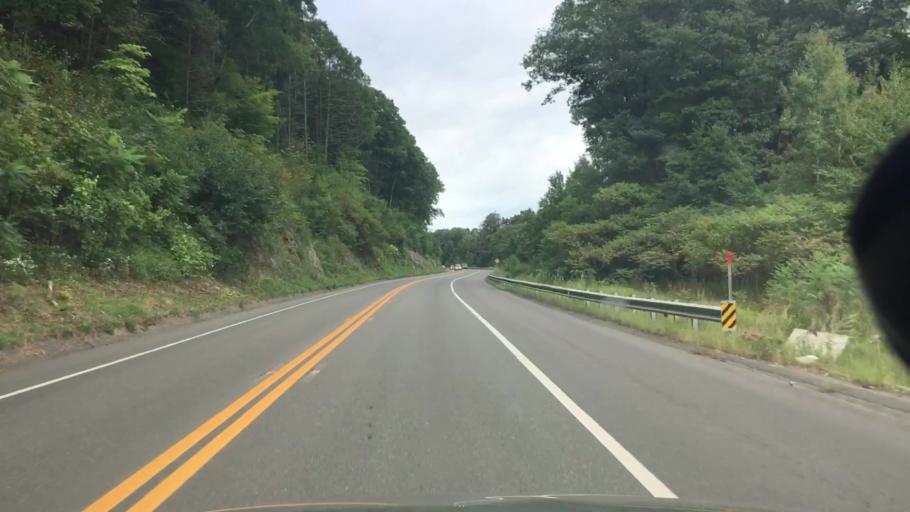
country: US
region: Massachusetts
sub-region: Franklin County
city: Greenfield
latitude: 42.5984
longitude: -72.6358
